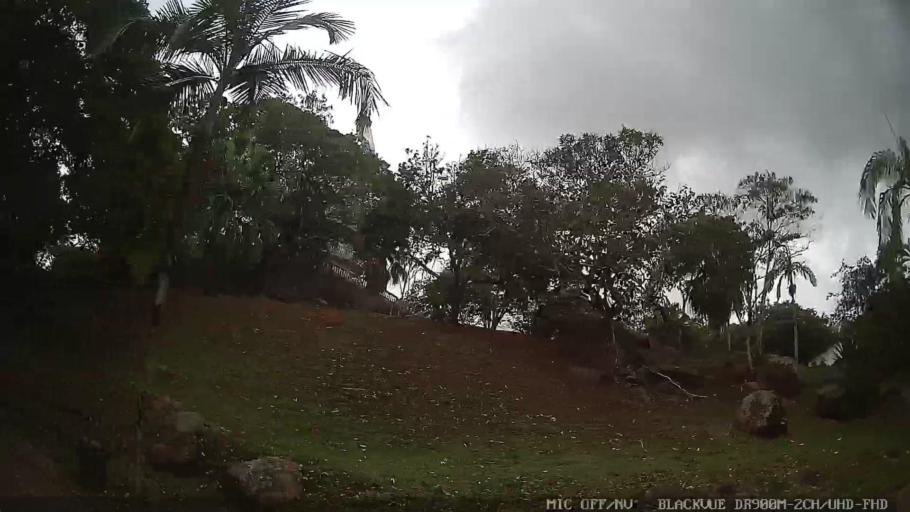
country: BR
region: Sao Paulo
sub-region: Salto
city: Salto
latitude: -23.2173
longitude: -47.2883
